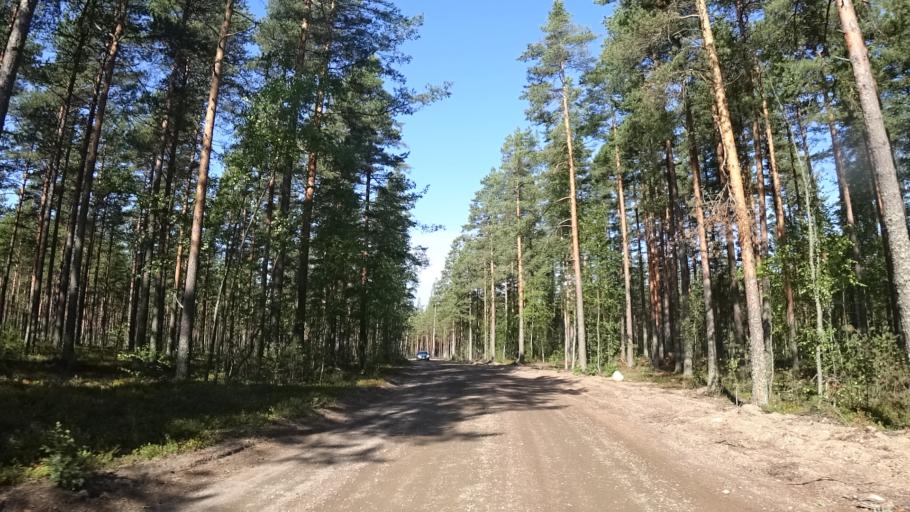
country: FI
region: Kymenlaakso
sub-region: Kotka-Hamina
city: Hamina
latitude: 60.5484
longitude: 27.2095
